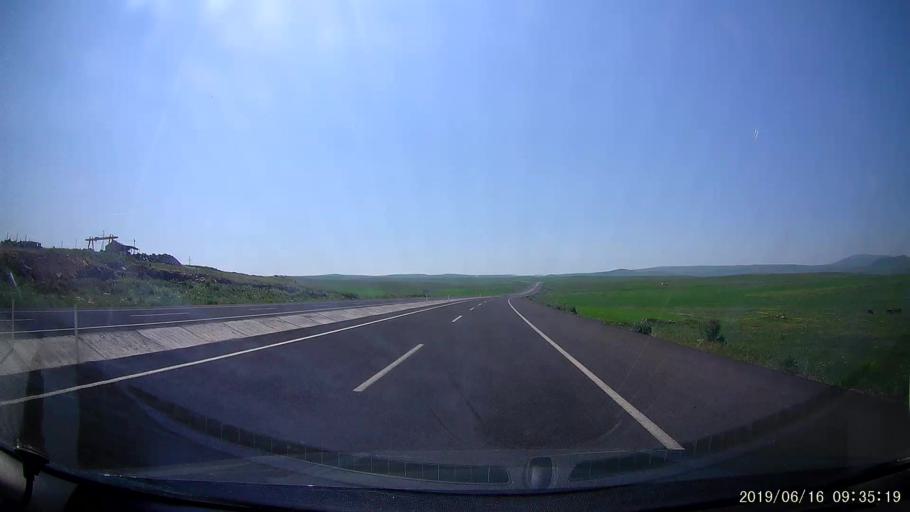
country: TR
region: Kars
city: Kars
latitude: 40.5738
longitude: 43.1538
